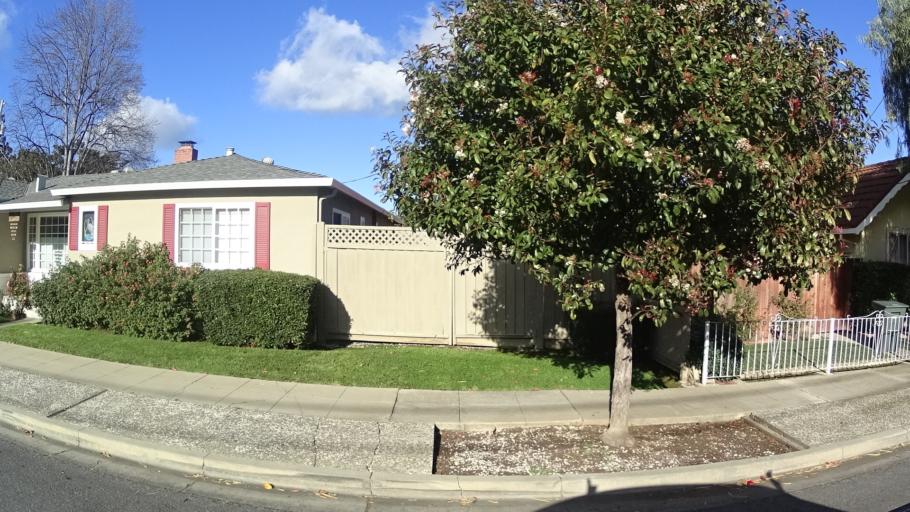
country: US
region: California
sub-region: Santa Clara County
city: Sunnyvale
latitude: 37.3751
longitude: -122.0448
